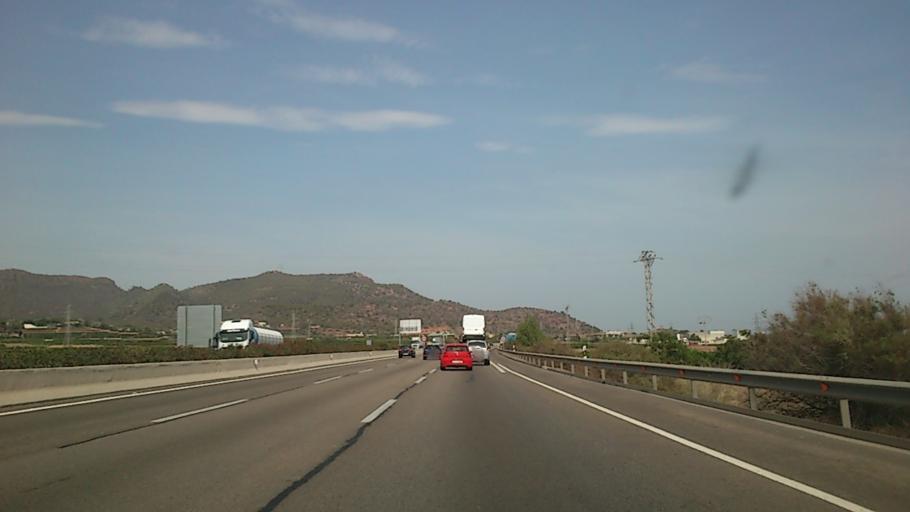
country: ES
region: Valencia
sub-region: Provincia de Valencia
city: Pucol
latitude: 39.6127
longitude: -0.3418
